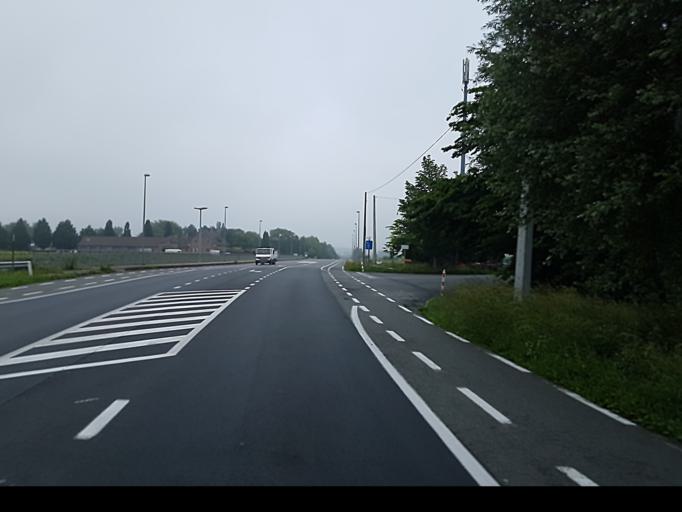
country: BE
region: Flanders
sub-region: Provincie West-Vlaanderen
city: Kortrijk
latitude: 50.7961
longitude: 3.2416
